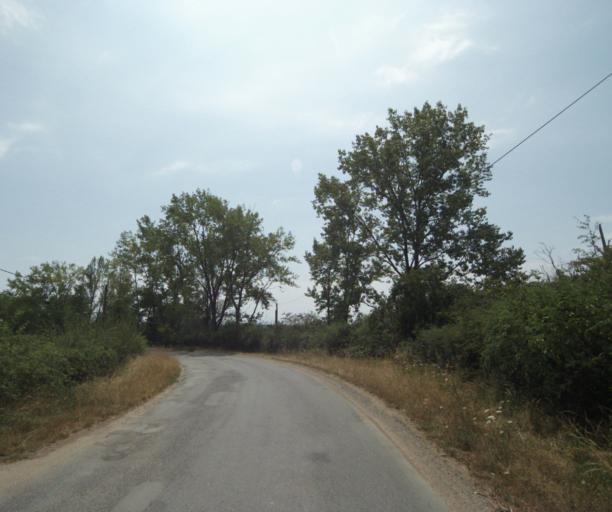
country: FR
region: Bourgogne
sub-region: Departement de Saone-et-Loire
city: Gueugnon
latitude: 46.5858
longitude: 4.0550
